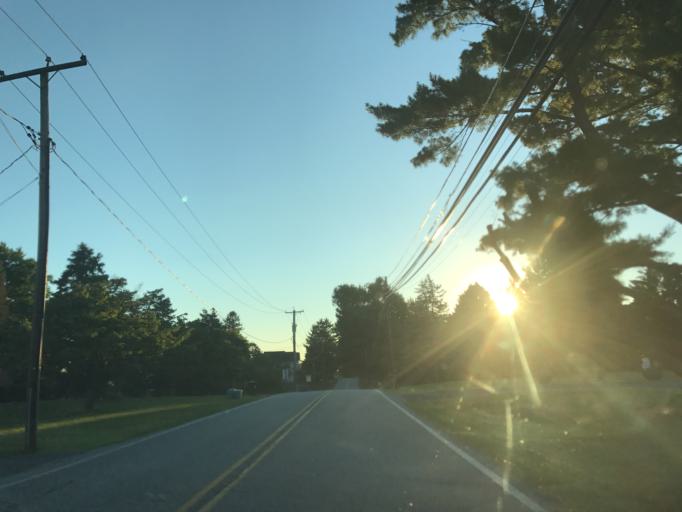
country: US
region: Maryland
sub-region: Harford County
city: Jarrettsville
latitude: 39.6008
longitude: -76.4856
